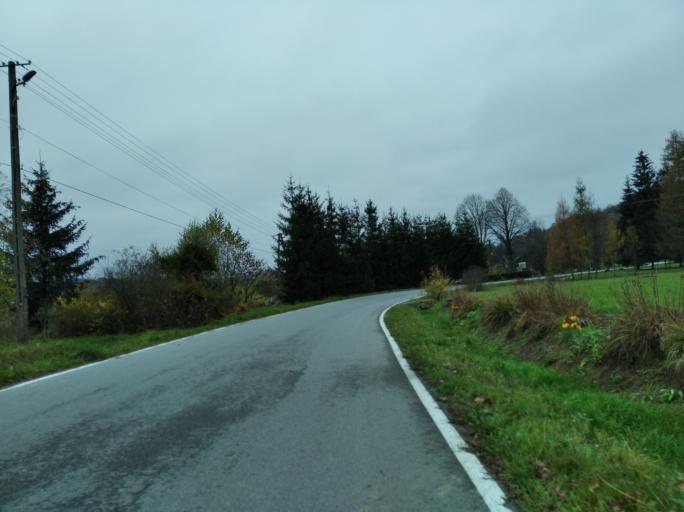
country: PL
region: Subcarpathian Voivodeship
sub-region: Powiat krosnienski
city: Leki
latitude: 49.8251
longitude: 21.6403
